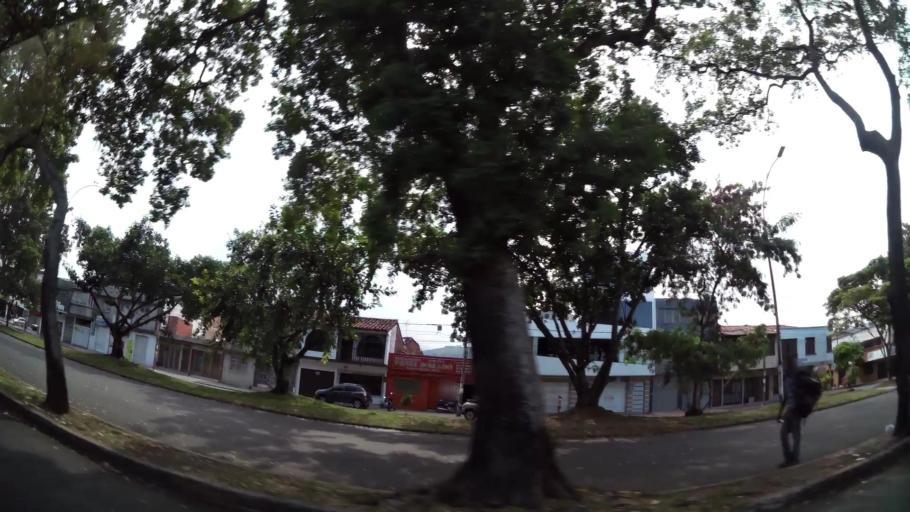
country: CO
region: Valle del Cauca
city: Cali
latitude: 3.4366
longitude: -76.5281
